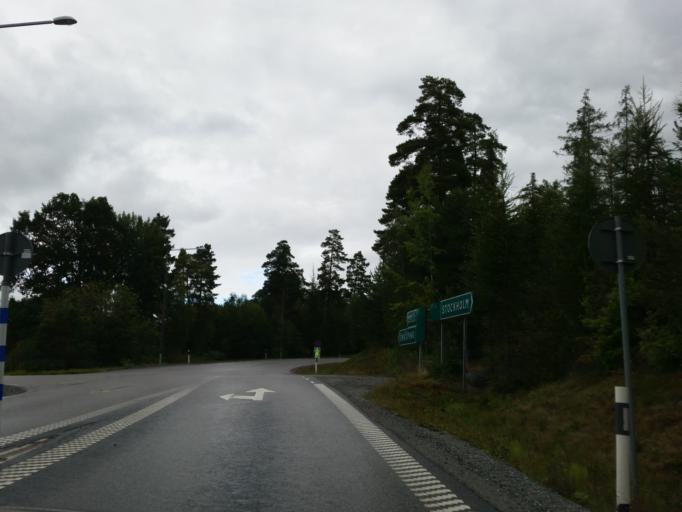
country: SE
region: Uppsala
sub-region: Enkopings Kommun
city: Dalby
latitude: 59.6205
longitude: 17.3923
